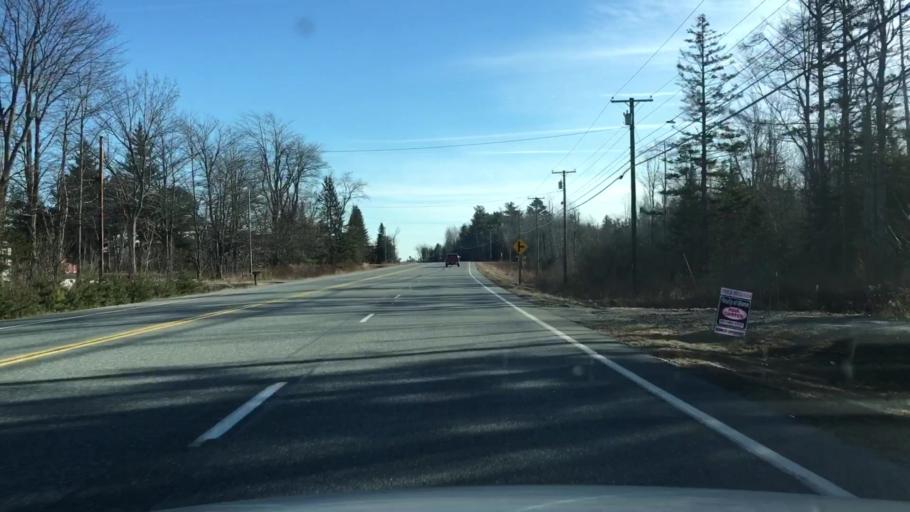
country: US
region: Maine
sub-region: Hancock County
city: Surry
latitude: 44.6230
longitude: -68.5318
